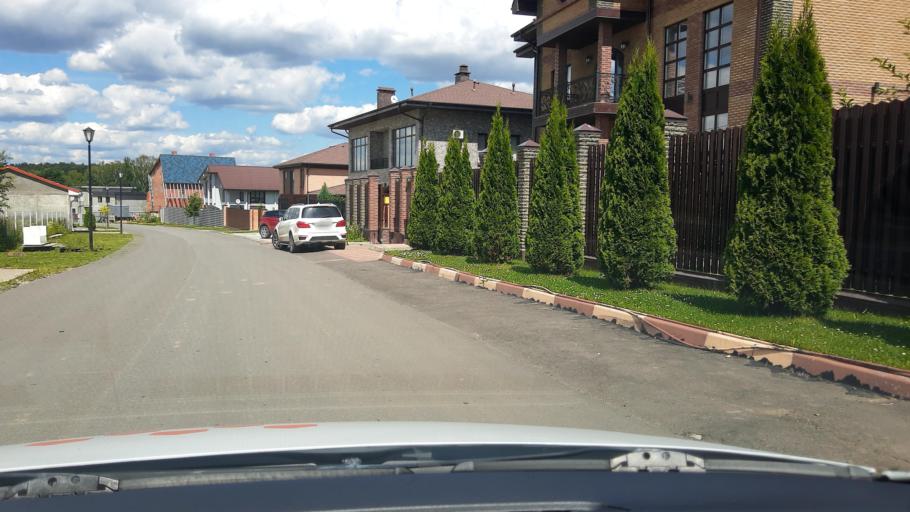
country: RU
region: Moskovskaya
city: Filimonki
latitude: 55.5445
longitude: 37.3378
